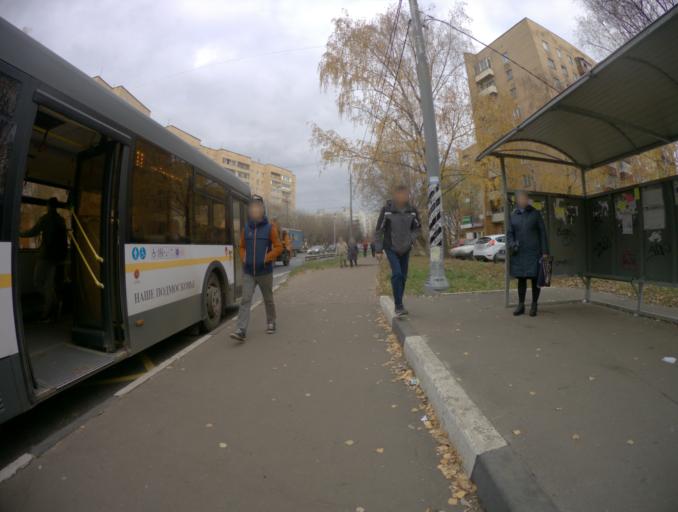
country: RU
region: Moskovskaya
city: Orekhovo-Zuyevo
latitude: 55.8066
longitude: 38.9685
